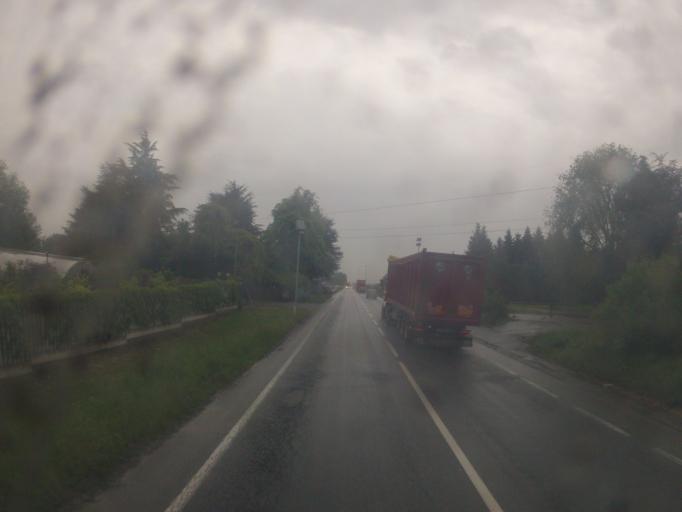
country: IT
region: Piedmont
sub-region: Provincia di Torino
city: La Loggia
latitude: 44.9351
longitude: 7.6714
